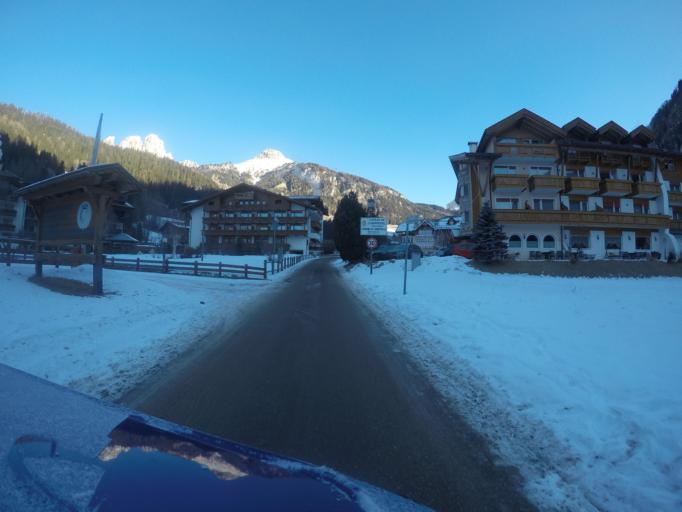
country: IT
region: Trentino-Alto Adige
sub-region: Provincia di Trento
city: Campitello di Fassa
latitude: 46.4725
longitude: 11.7356
